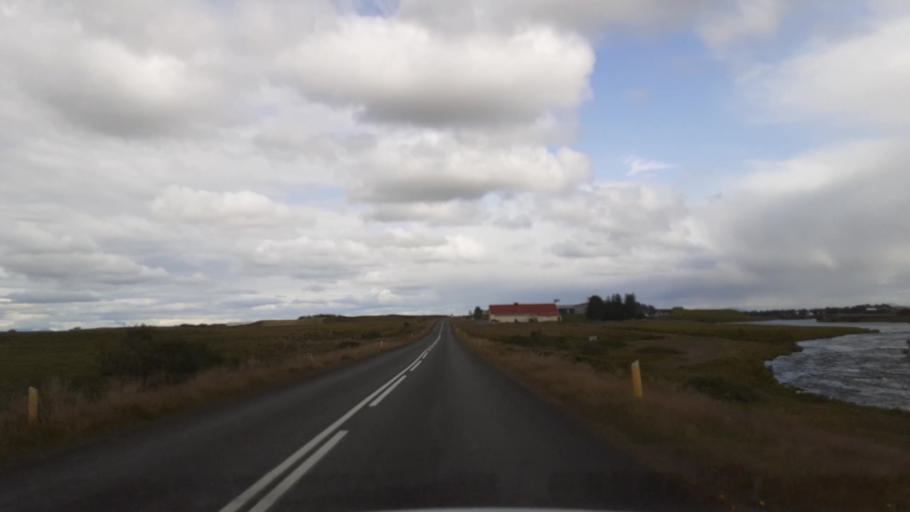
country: IS
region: South
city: Vestmannaeyjar
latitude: 63.8286
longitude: -20.4258
